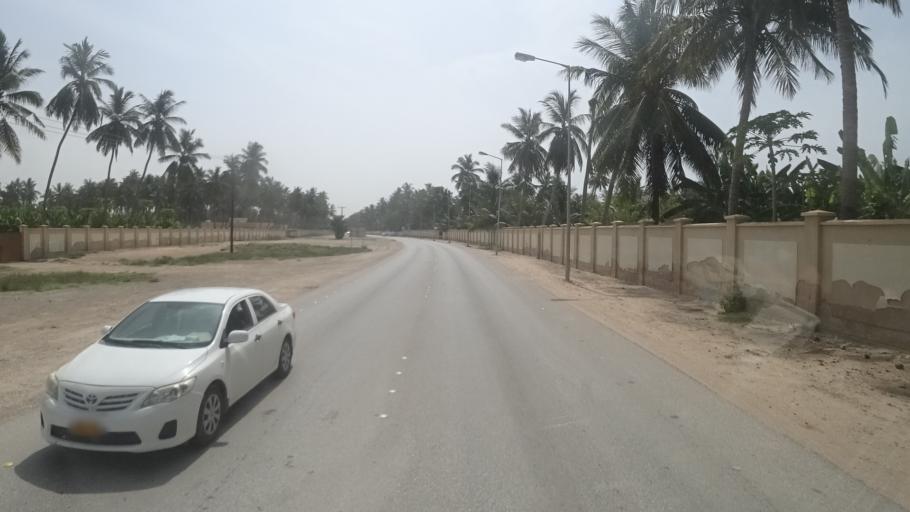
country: OM
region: Zufar
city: Salalah
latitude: 17.0139
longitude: 54.1488
